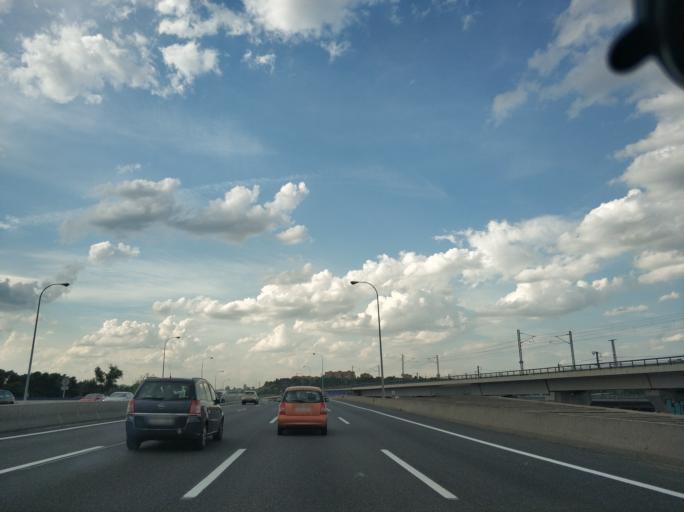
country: ES
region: Madrid
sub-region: Provincia de Madrid
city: Villaverde
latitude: 40.3658
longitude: -3.6782
